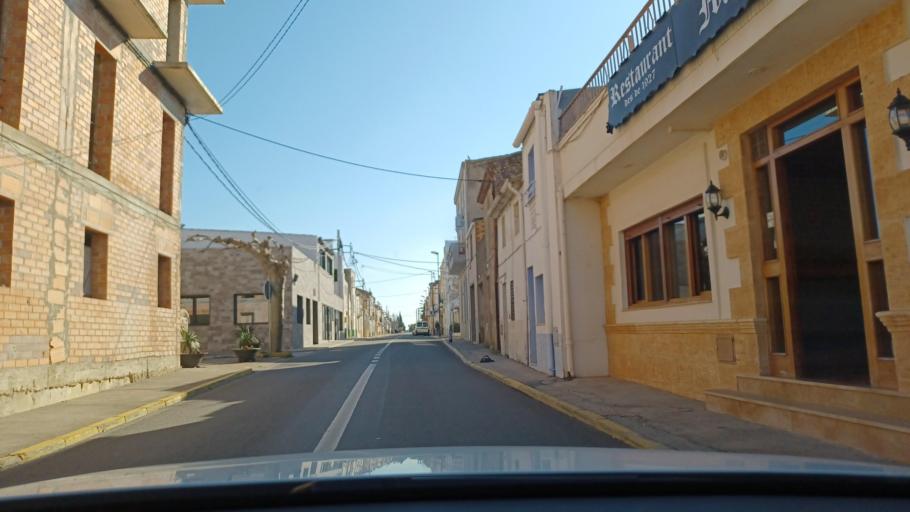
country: ES
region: Catalonia
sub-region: Provincia de Tarragona
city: Ulldecona
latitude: 40.6278
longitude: 0.3653
